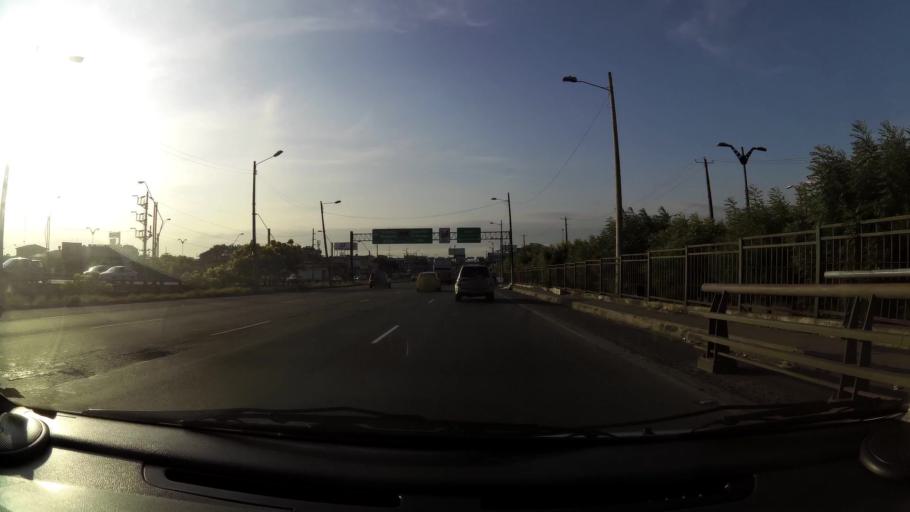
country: EC
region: Guayas
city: Eloy Alfaro
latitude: -2.1644
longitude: -79.8467
